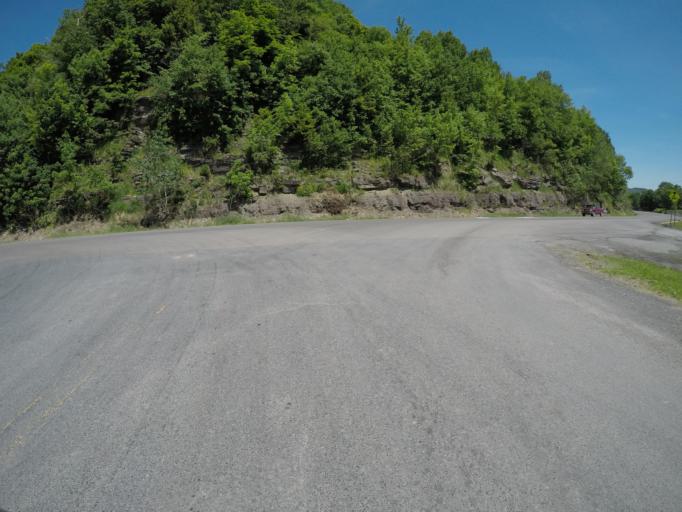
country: US
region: New York
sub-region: Delaware County
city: Walton
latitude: 42.1617
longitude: -75.0462
